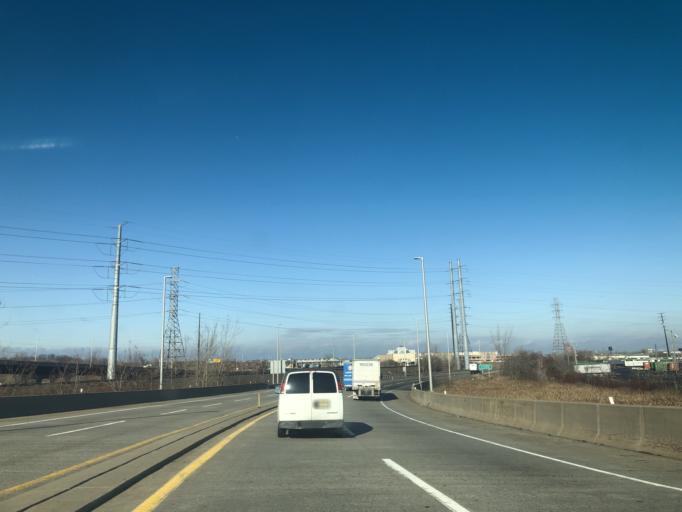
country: US
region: New Jersey
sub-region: Hudson County
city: Jersey City
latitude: 40.7522
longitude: -74.0691
